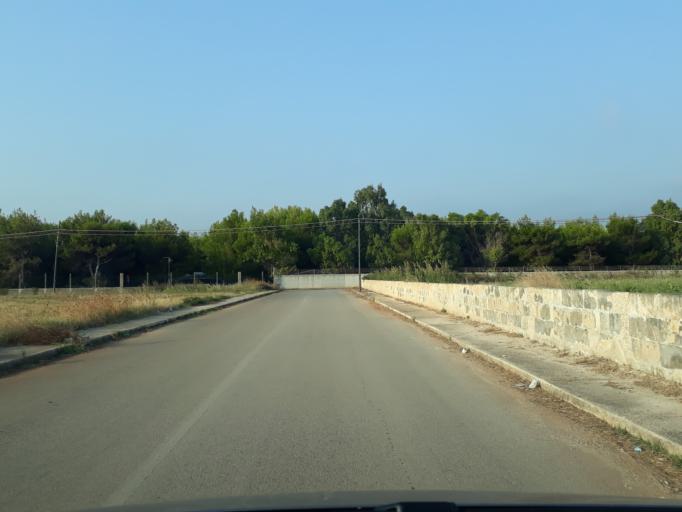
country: IT
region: Apulia
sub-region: Provincia di Brindisi
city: Carovigno
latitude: 40.7495
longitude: 17.7131
